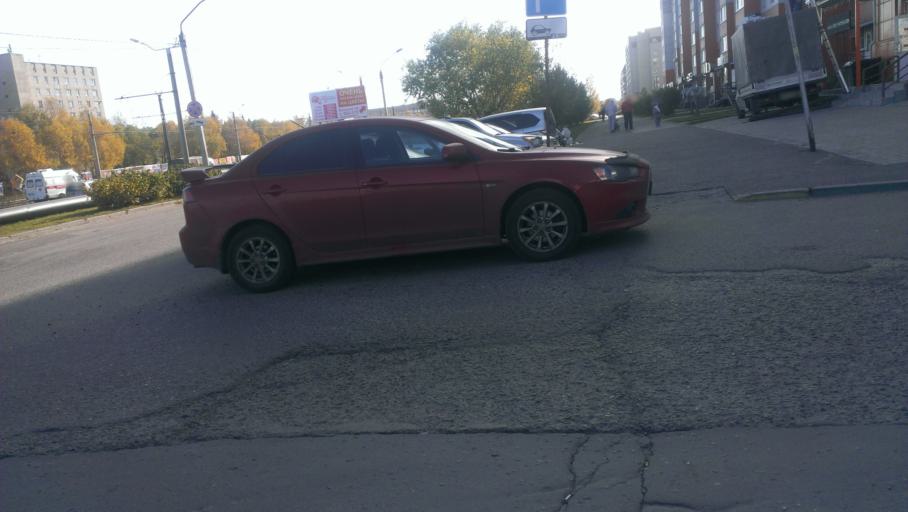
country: RU
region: Altai Krai
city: Novosilikatnyy
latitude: 53.3360
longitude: 83.6933
